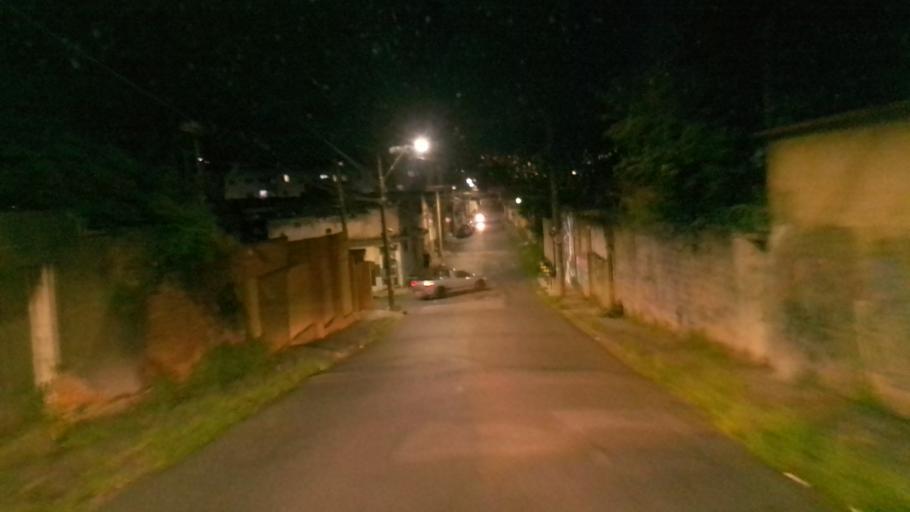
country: BR
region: Minas Gerais
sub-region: Belo Horizonte
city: Belo Horizonte
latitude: -19.9039
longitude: -43.9564
